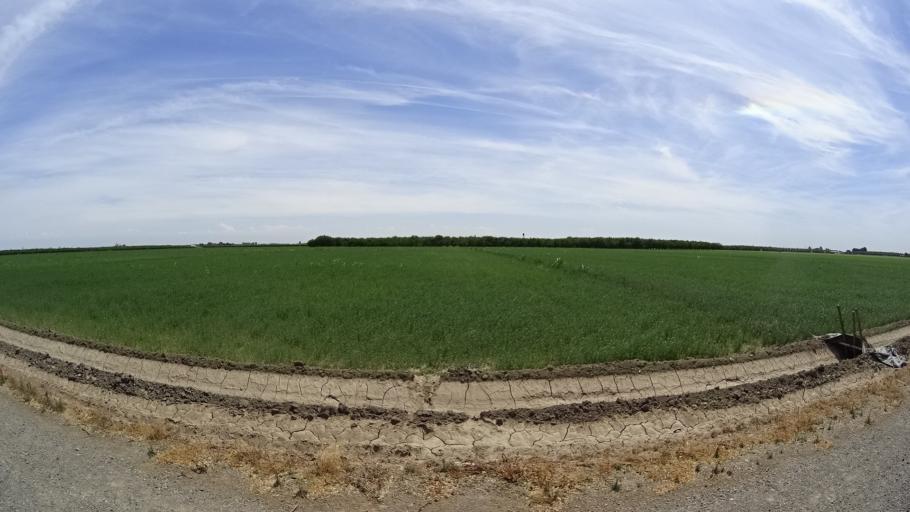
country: US
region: California
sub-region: Kings County
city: Lucerne
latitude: 36.3814
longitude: -119.6910
